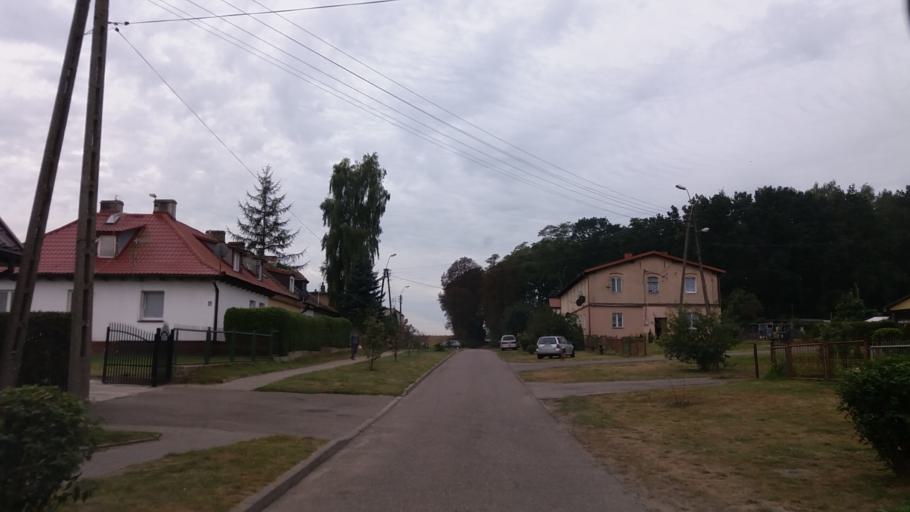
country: PL
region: West Pomeranian Voivodeship
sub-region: Powiat choszczenski
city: Pelczyce
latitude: 53.0882
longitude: 15.2986
